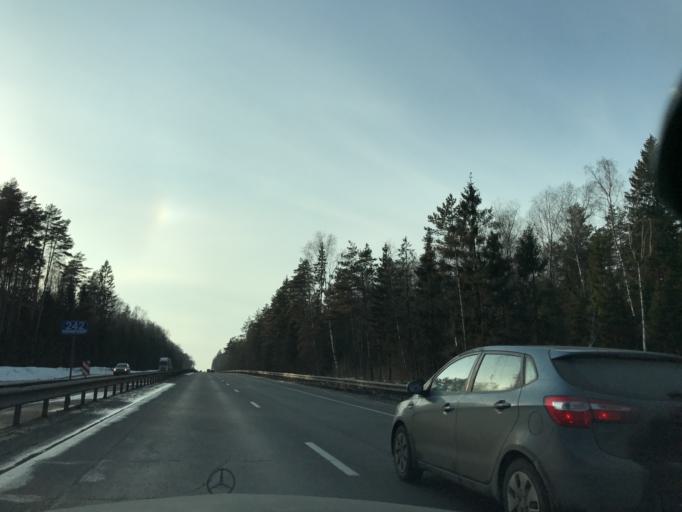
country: RU
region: Vladimir
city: Melekhovo
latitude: 56.2094
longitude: 41.2672
